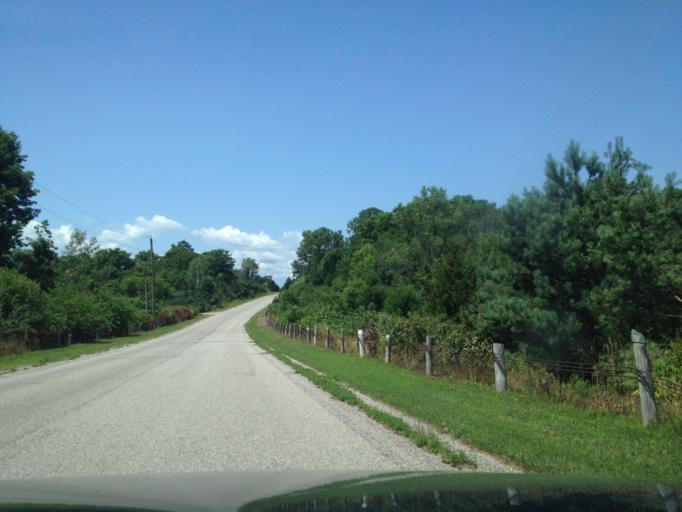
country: CA
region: Ontario
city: Aylmer
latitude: 42.6448
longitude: -80.7914
